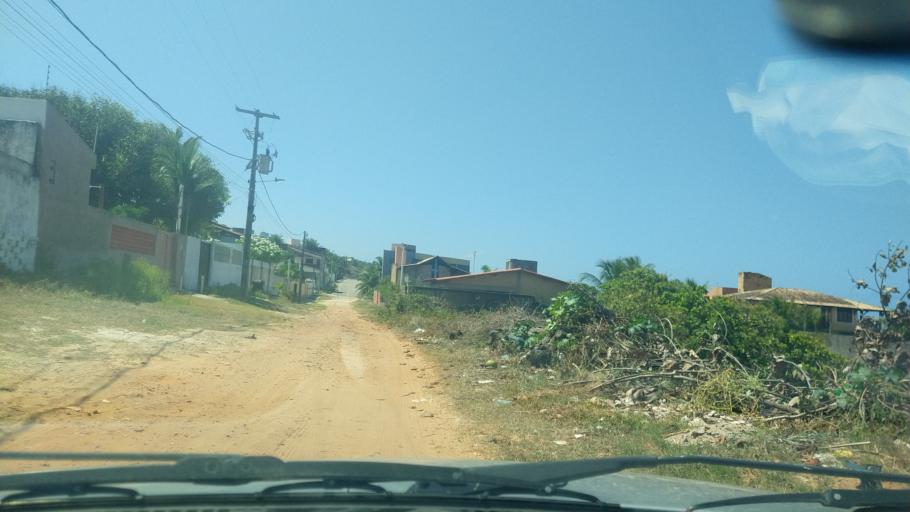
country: BR
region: Rio Grande do Norte
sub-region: Parnamirim
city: Parnamirim
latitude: -5.9526
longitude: -35.1529
